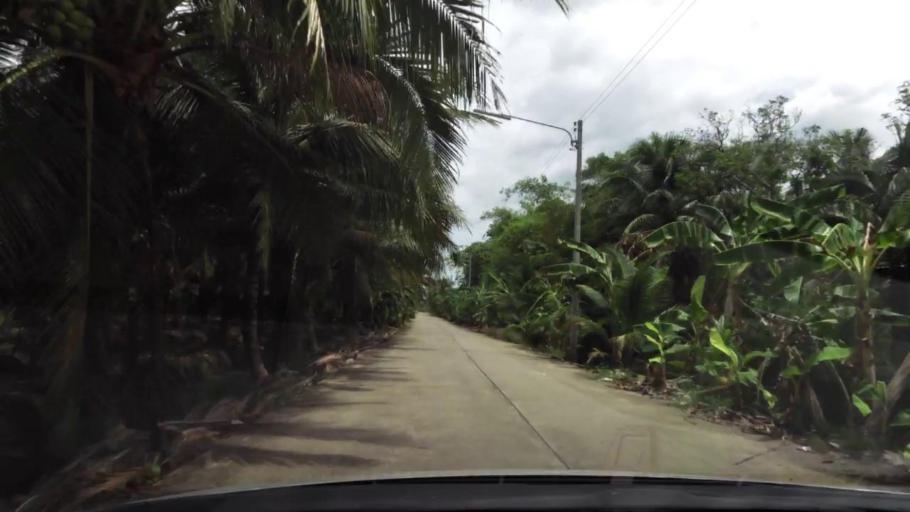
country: TH
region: Ratchaburi
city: Damnoen Saduak
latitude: 13.5307
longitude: 100.0018
